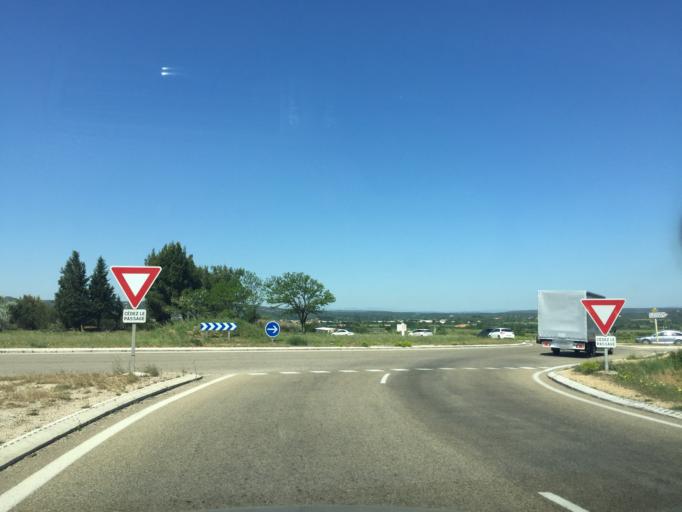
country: FR
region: Languedoc-Roussillon
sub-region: Departement du Gard
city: Remoulins
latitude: 43.9400
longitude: 4.5978
